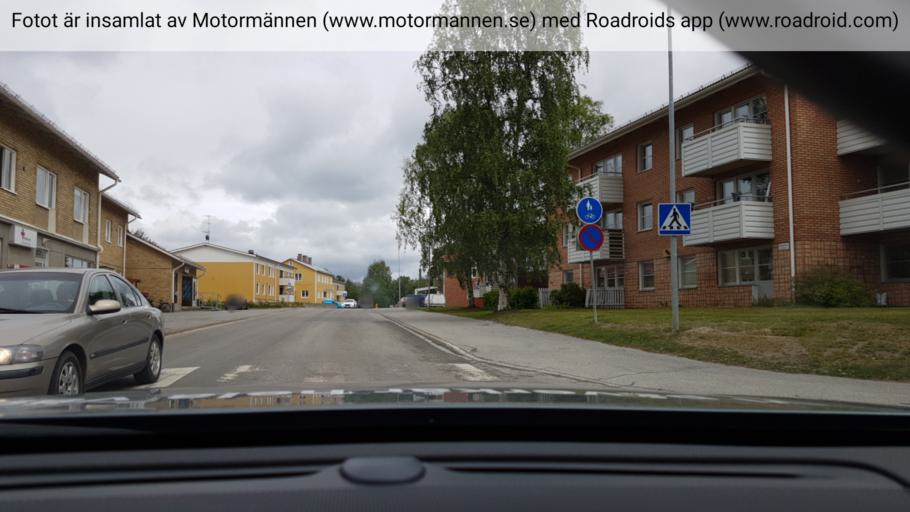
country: SE
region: Vaesterbotten
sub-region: Lycksele Kommun
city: Lycksele
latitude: 64.5922
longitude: 18.6720
